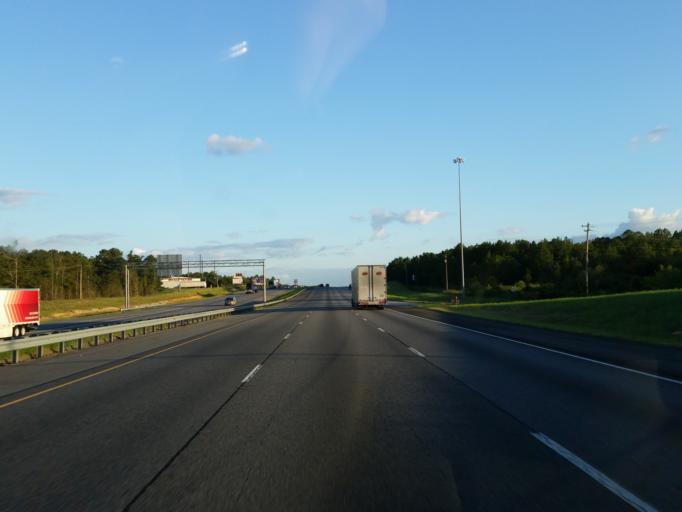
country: US
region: Georgia
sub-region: Crisp County
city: Cordele
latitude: 31.9059
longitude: -83.7374
